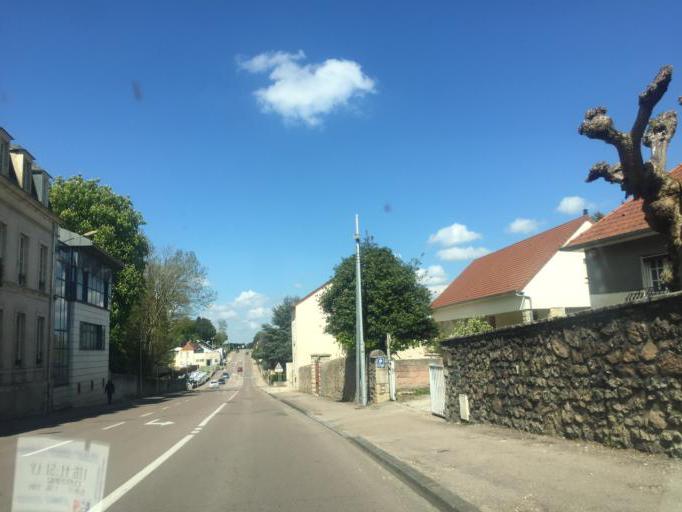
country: FR
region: Bourgogne
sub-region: Departement de l'Yonne
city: Avallon
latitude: 47.4932
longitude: 3.9071
